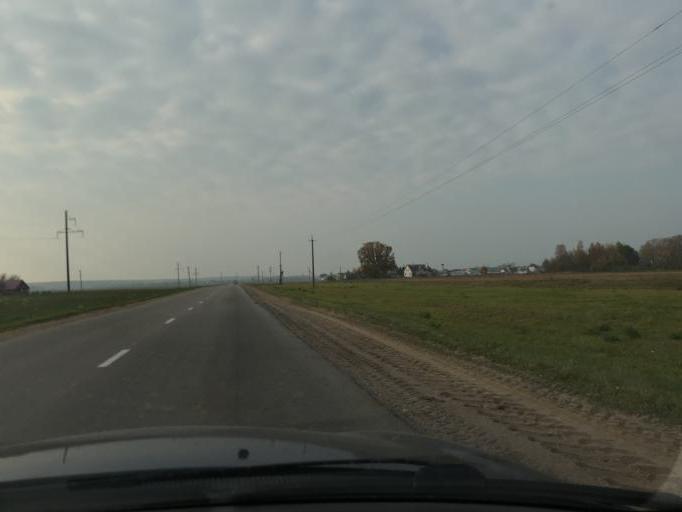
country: BY
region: Grodnenskaya
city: Lida
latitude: 53.8579
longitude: 25.3047
